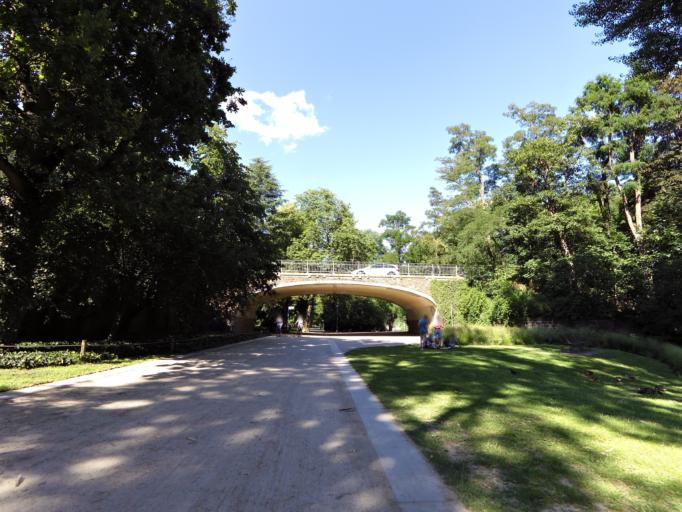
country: DE
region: Rheinland-Pfalz
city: Koblenz
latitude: 50.3420
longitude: 7.5887
